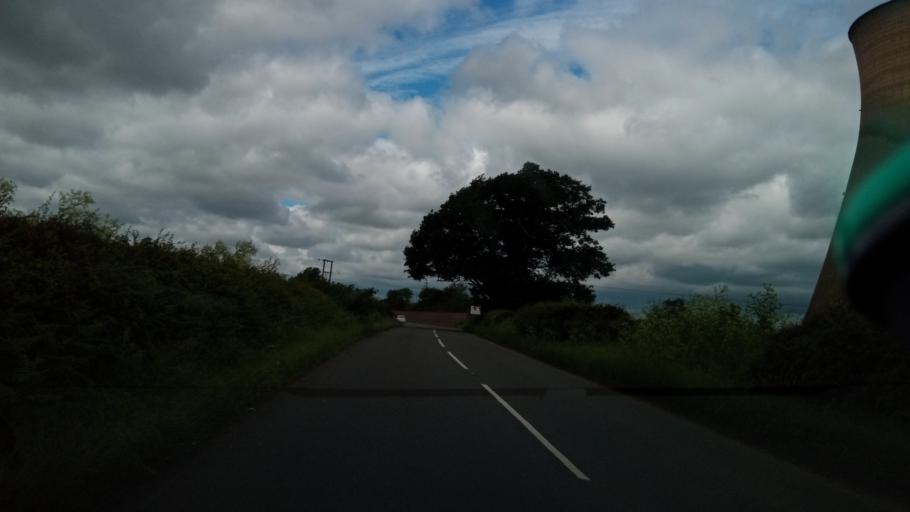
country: GB
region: England
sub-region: Derbyshire
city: Findern
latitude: 52.8543
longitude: -1.5379
